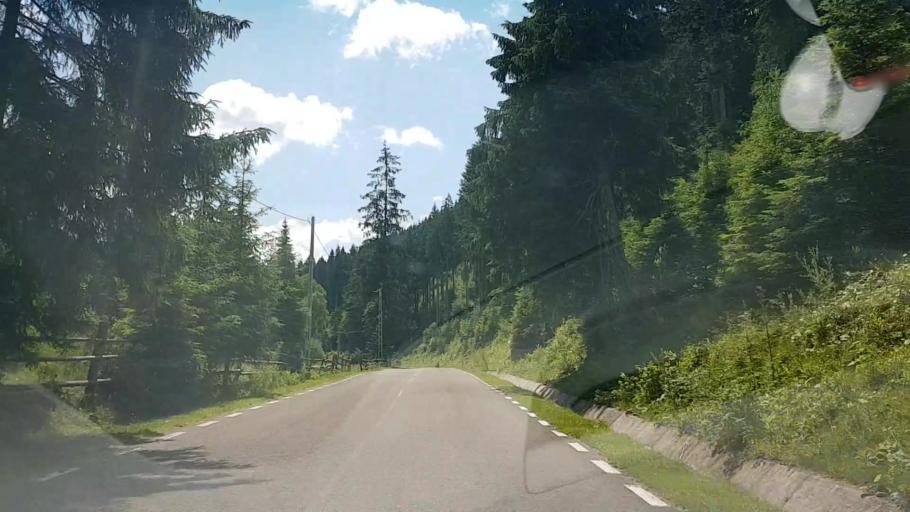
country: RO
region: Suceava
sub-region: Comuna Sadova
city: Sadova
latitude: 47.4809
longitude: 25.4927
